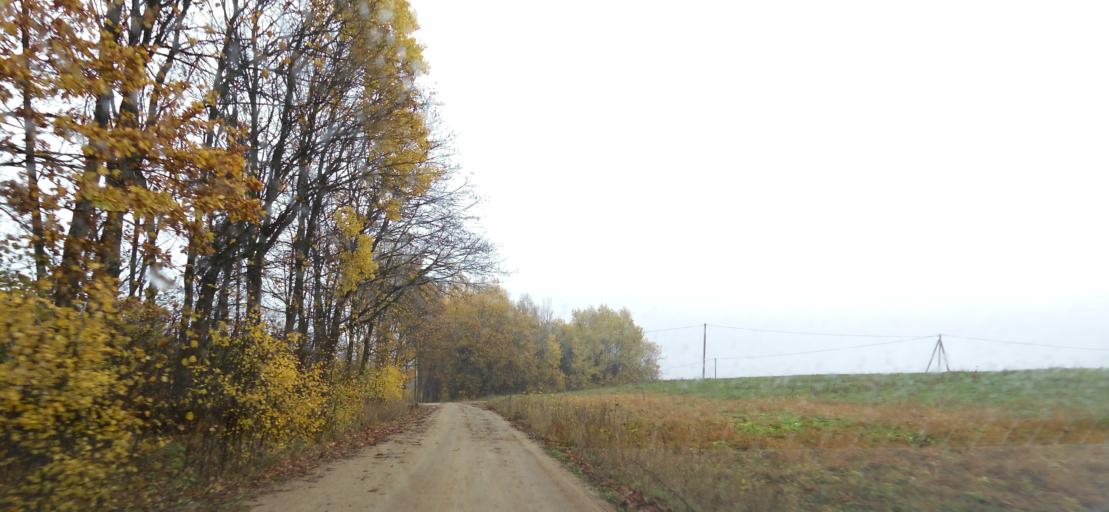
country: LT
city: Skaidiskes
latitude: 54.6270
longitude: 25.4769
